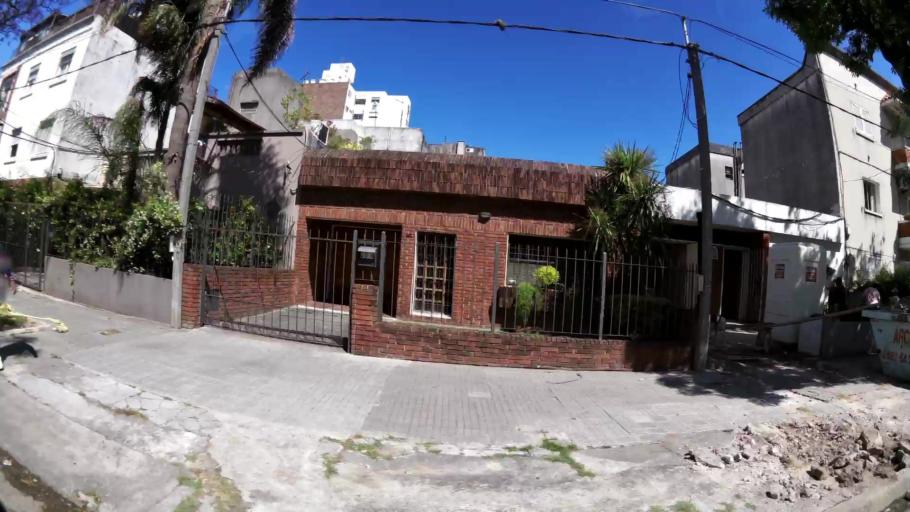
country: UY
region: Montevideo
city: Montevideo
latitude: -34.9056
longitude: -56.1479
